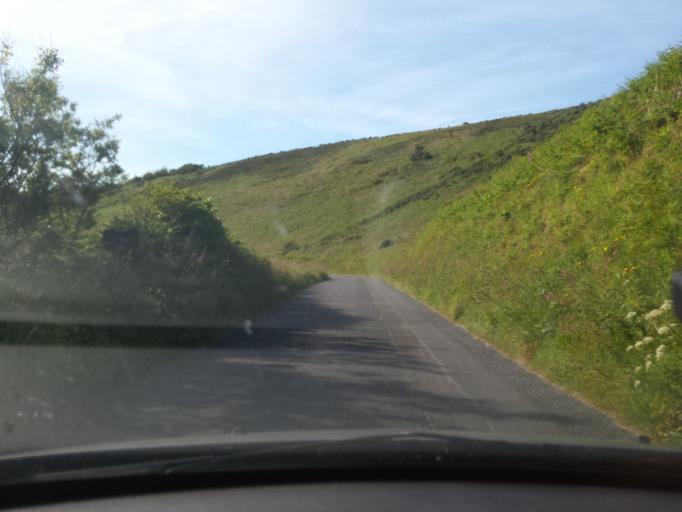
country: FR
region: Lower Normandy
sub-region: Departement de la Manche
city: Beaumont-Hague
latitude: 49.6895
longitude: -1.9325
